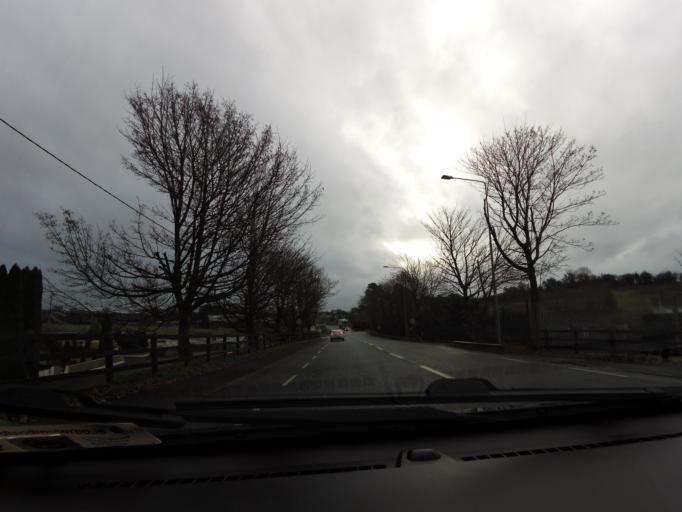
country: IE
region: Munster
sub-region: North Tipperary
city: Roscrea
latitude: 52.9600
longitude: -7.8045
